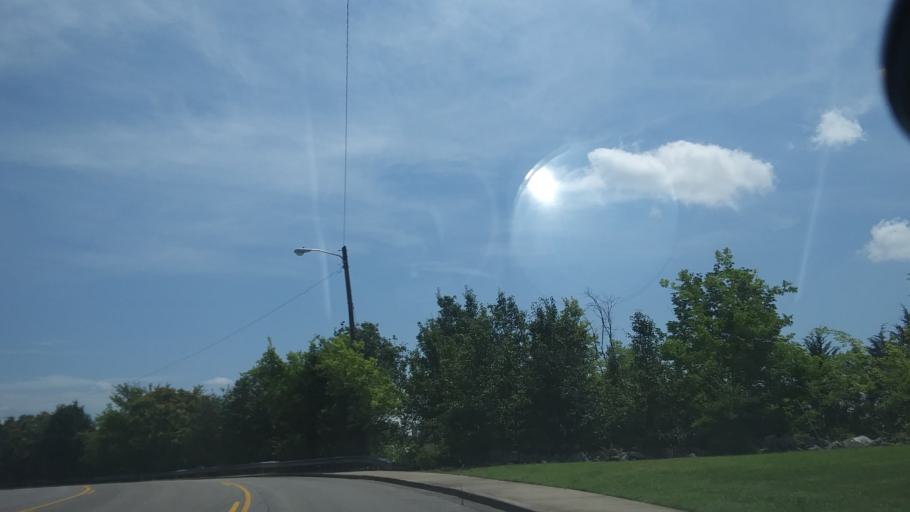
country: US
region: Tennessee
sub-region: Rutherford County
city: La Vergne
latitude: 36.0662
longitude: -86.6330
